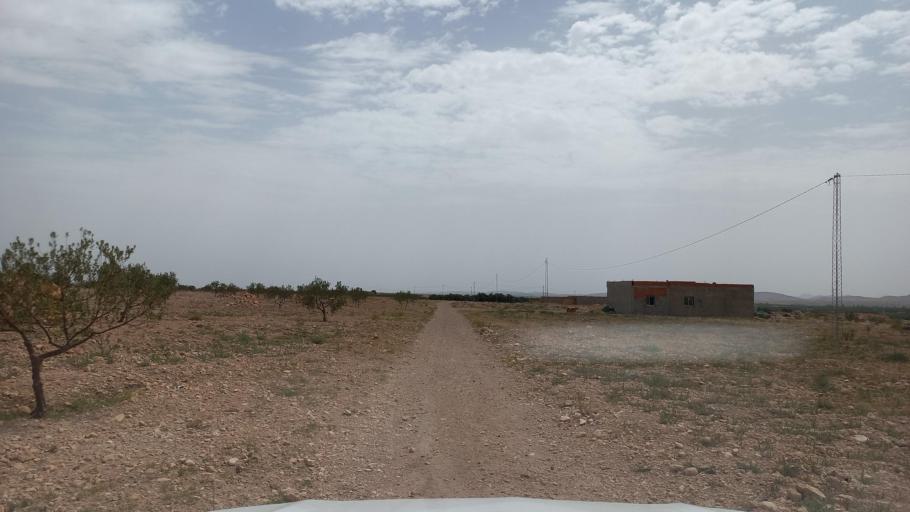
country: TN
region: Al Qasrayn
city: Kasserine
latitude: 35.2911
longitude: 9.0022
